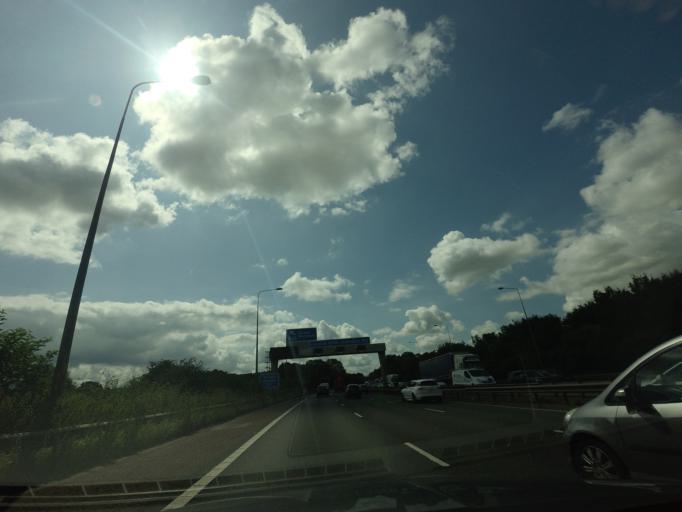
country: GB
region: England
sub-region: Lancashire
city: Clayton-le-Woods
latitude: 53.7312
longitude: -2.6482
